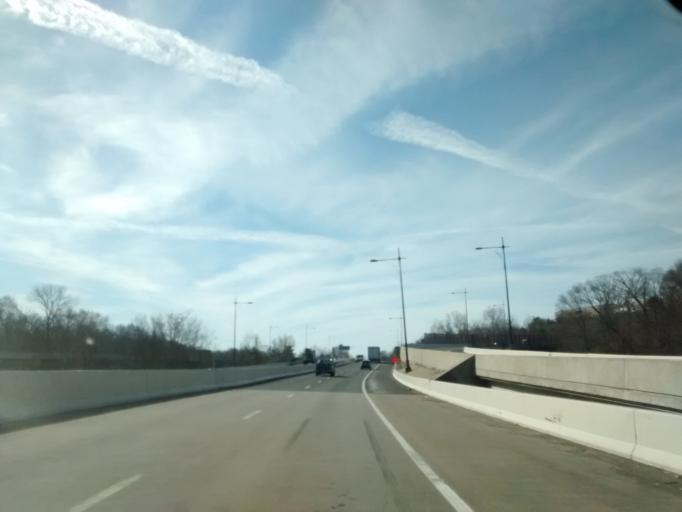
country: US
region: Massachusetts
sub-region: Worcester County
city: Millbury
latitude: 42.2018
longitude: -71.7760
